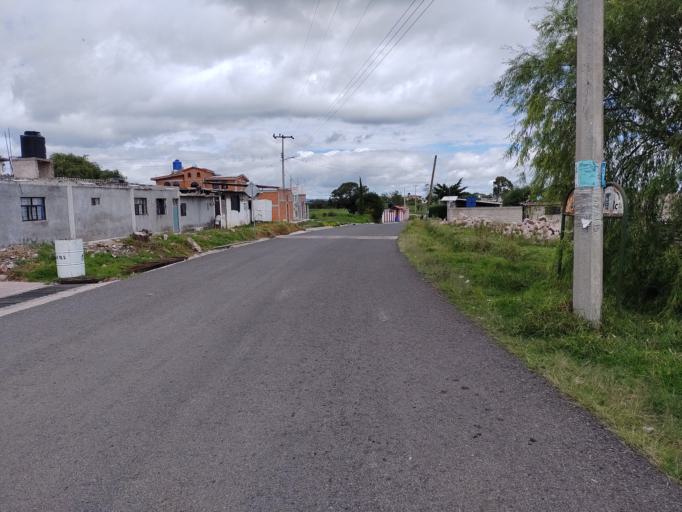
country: MX
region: Mexico
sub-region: Aculco
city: Gunyo Poniente (San Jose Gunyo)
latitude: 20.1158
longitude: -99.8745
